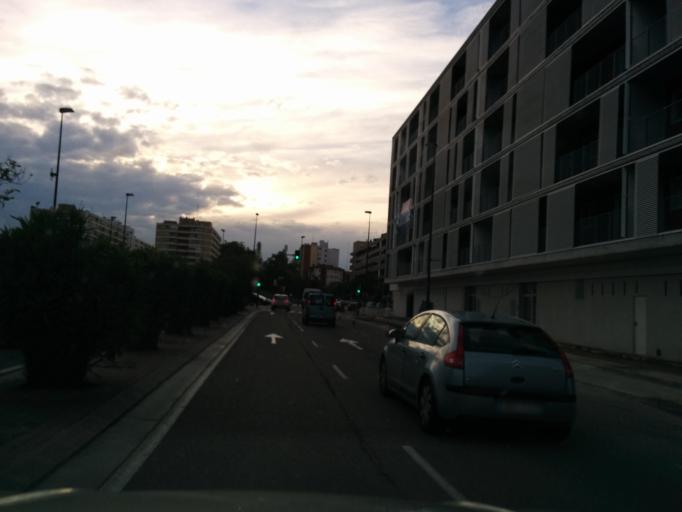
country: ES
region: Aragon
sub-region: Provincia de Zaragoza
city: Zaragoza
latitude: 41.6365
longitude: -0.8663
